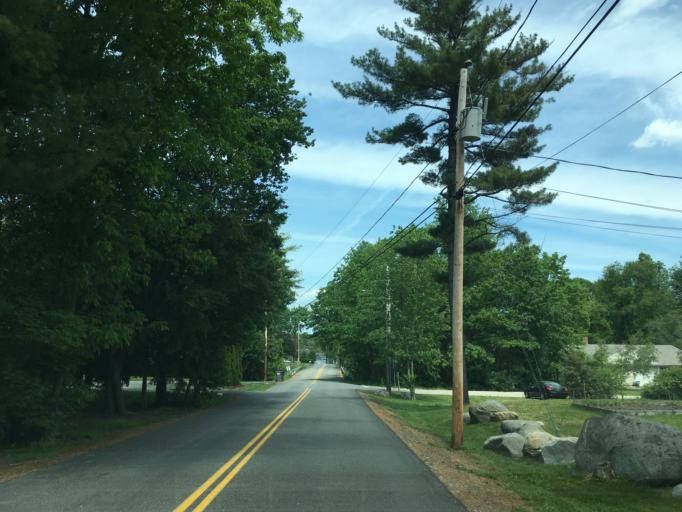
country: US
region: New Hampshire
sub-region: Rockingham County
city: Stratham Station
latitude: 43.0349
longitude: -70.8703
